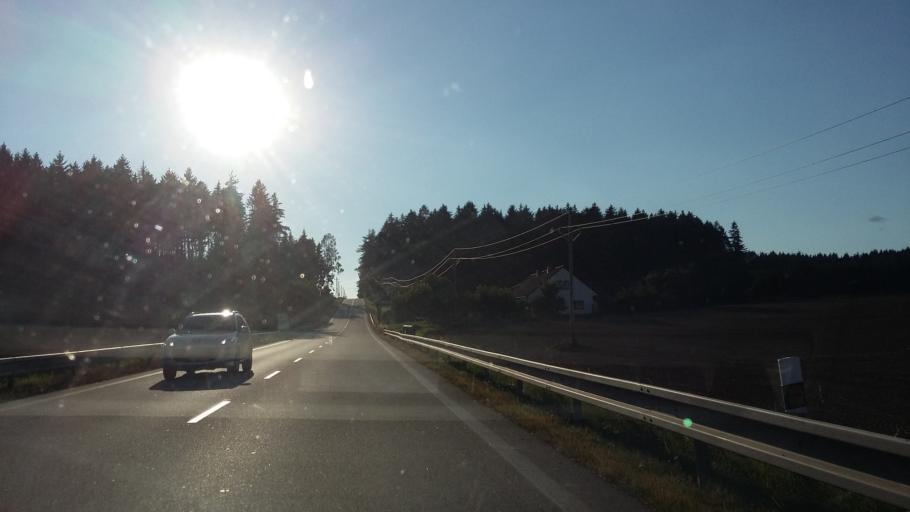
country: CZ
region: Vysocina
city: Luka nad Jihlavou
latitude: 49.3988
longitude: 15.6965
